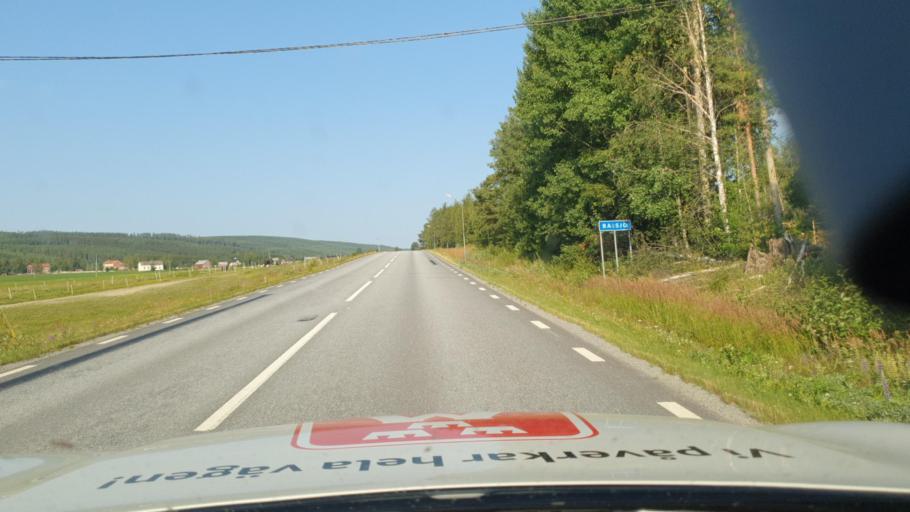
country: SE
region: Vaesterbotten
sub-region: Bjurholms Kommun
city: Bjurholm
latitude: 63.9257
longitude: 19.0779
